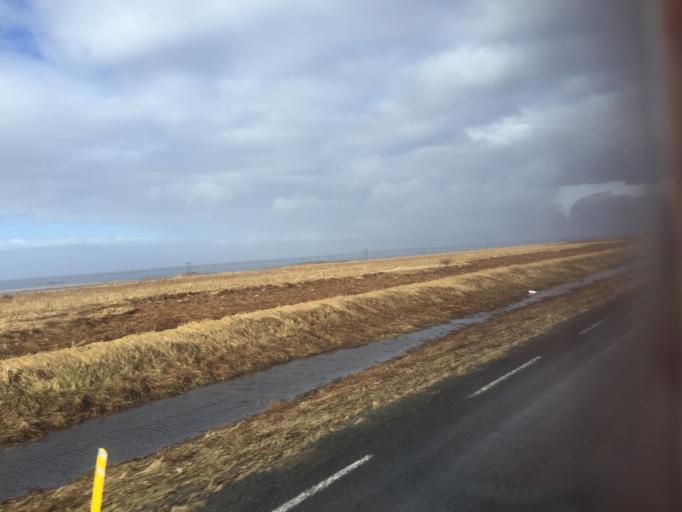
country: IS
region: West
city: Borgarnes
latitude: 64.4435
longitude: -21.9587
